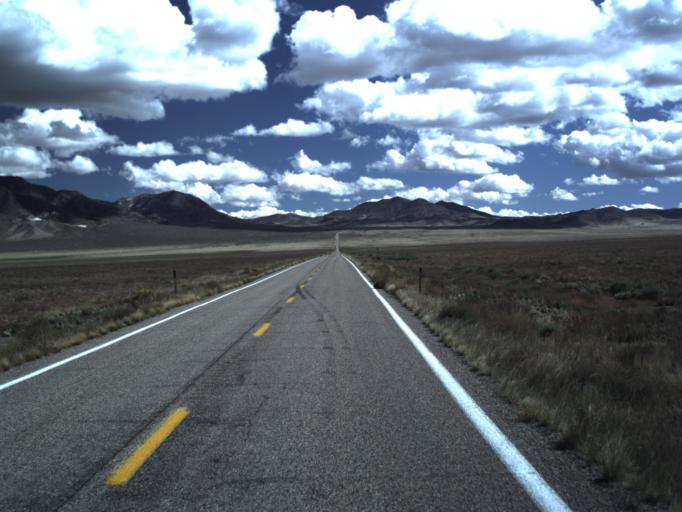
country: US
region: Utah
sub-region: Beaver County
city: Milford
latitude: 38.4660
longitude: -113.3932
